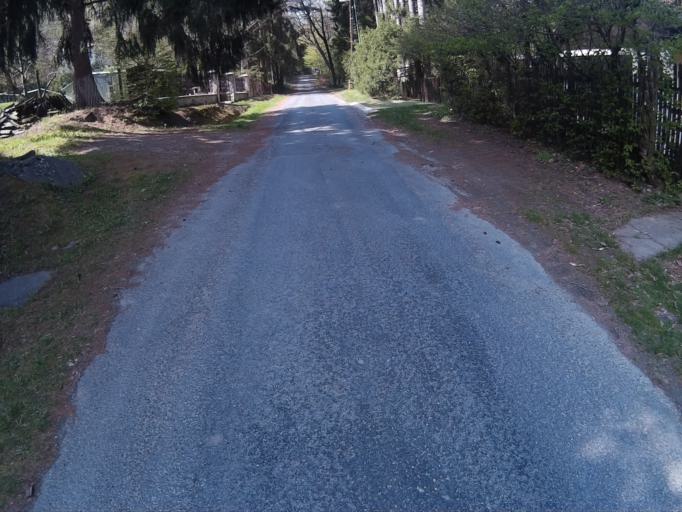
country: AT
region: Burgenland
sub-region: Politischer Bezirk Oberwart
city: Rechnitz
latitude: 47.3465
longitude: 16.4863
